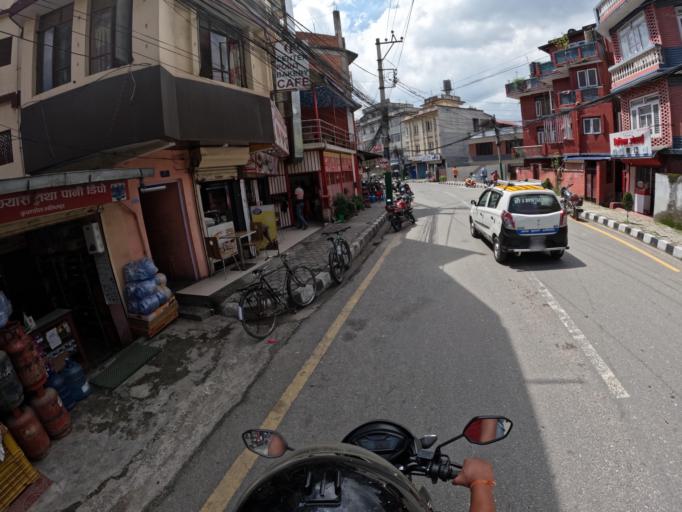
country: NP
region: Central Region
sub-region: Bagmati Zone
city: Patan
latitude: 27.6866
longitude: 85.3153
